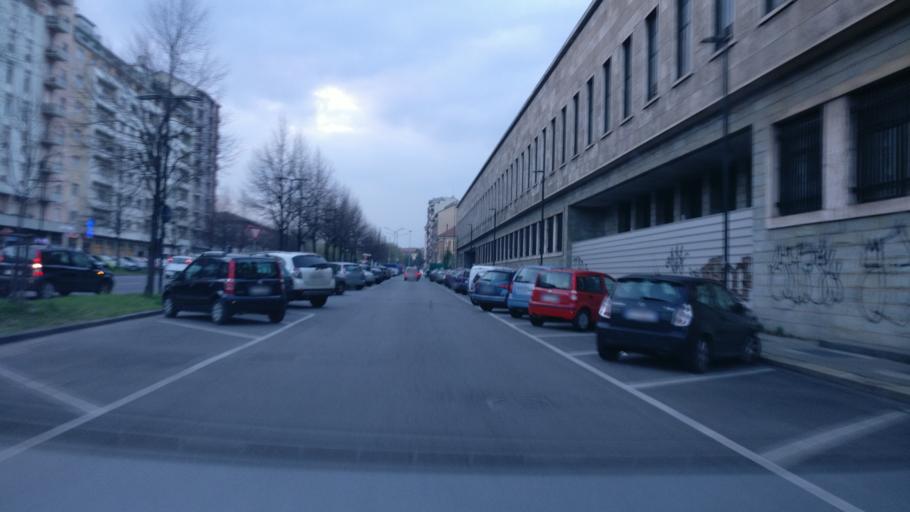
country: IT
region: Piedmont
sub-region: Provincia di Torino
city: Turin
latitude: 45.0457
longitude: 7.6641
